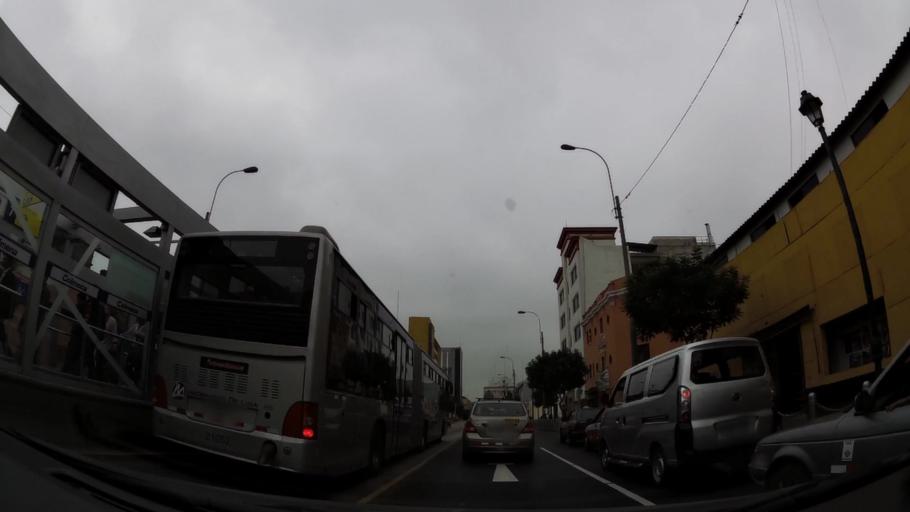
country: PE
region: Lima
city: Lima
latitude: -12.0523
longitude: -77.0328
